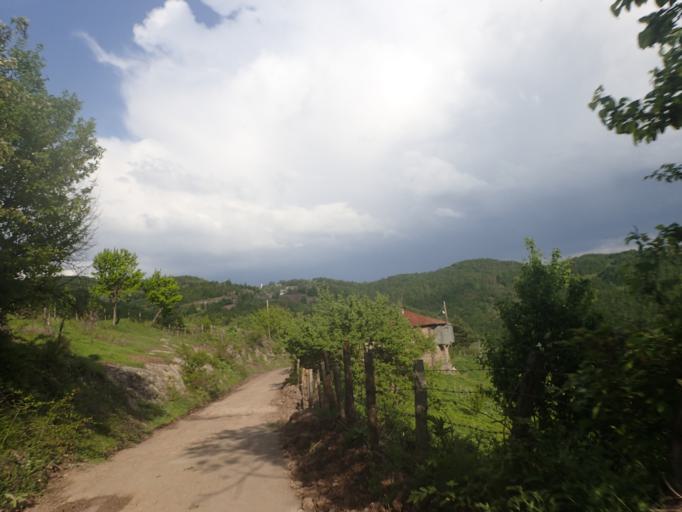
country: TR
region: Ordu
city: Akkus
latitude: 40.8223
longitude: 36.9411
